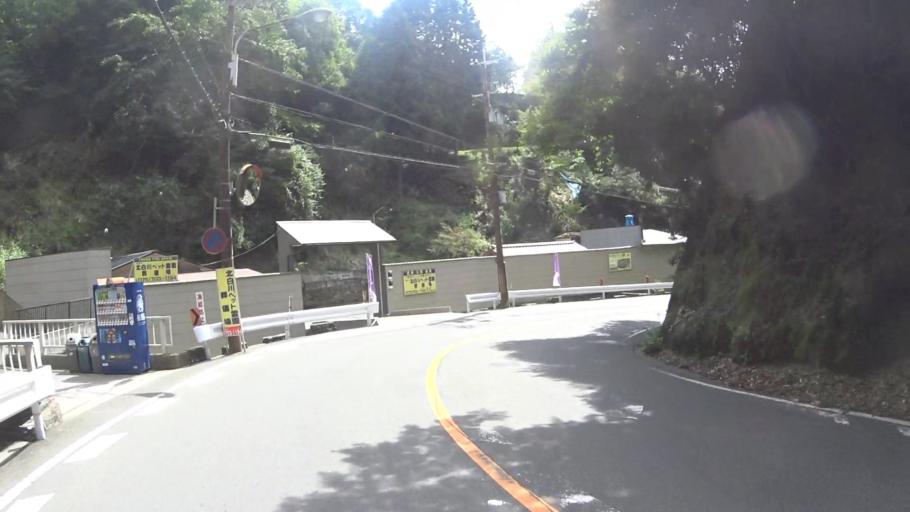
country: JP
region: Kyoto
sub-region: Kyoto-shi
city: Kamigyo-ku
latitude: 35.0342
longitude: 135.8092
